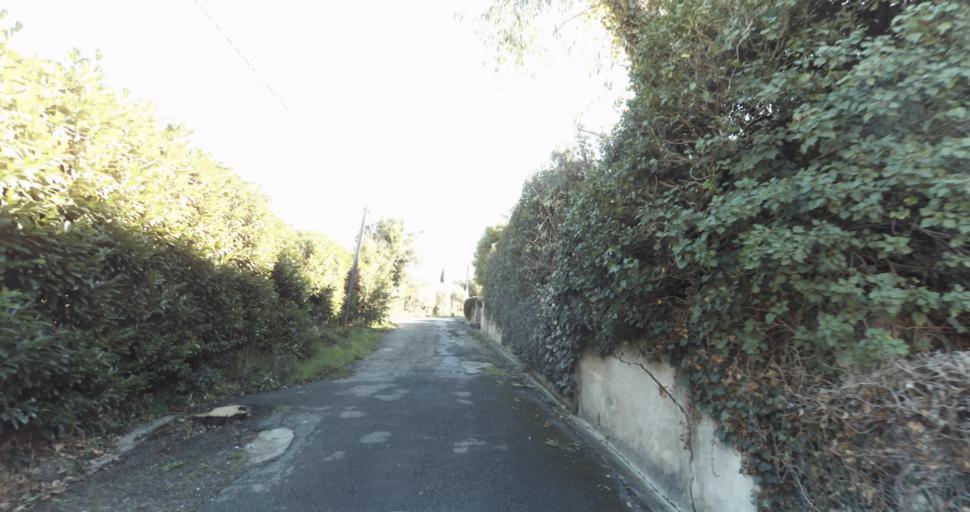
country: FR
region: Provence-Alpes-Cote d'Azur
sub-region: Departement des Alpes-Maritimes
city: Saint-Paul-de-Vence
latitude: 43.7064
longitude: 7.1278
